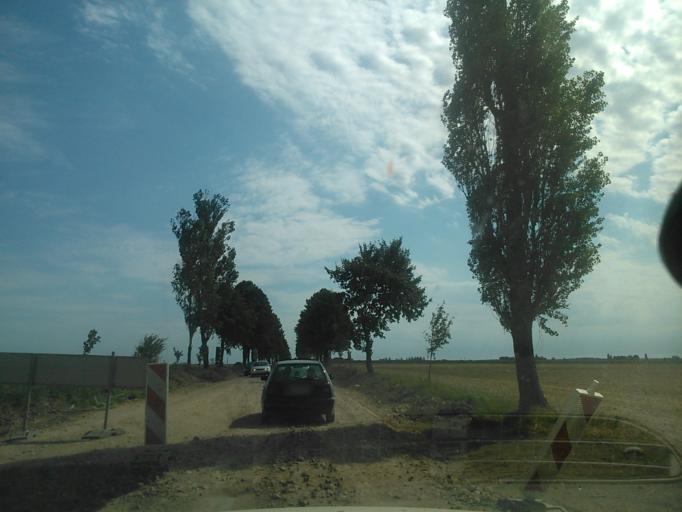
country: PL
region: Warmian-Masurian Voivodeship
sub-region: Powiat dzialdowski
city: Ilowo -Osada
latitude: 53.1857
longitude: 20.2850
